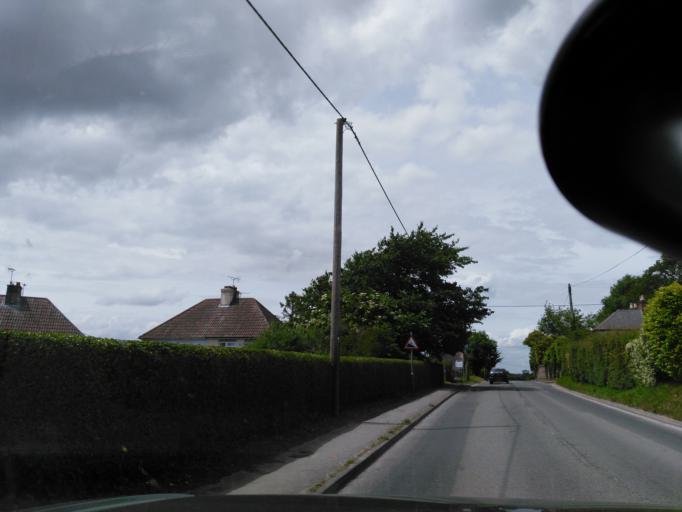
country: GB
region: England
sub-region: Wiltshire
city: Shrewton
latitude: 51.1901
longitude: -1.8996
